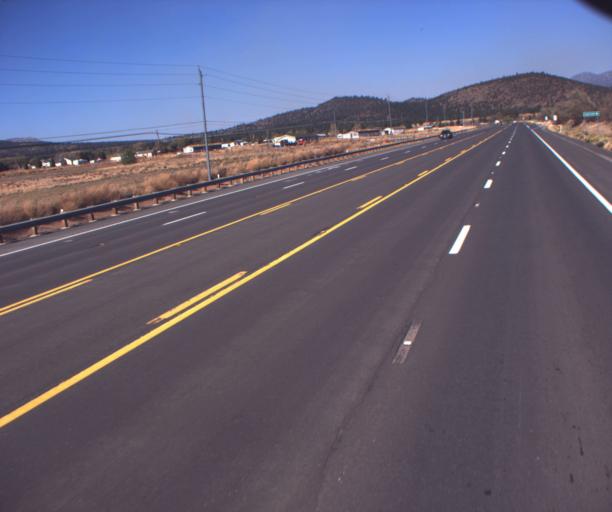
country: US
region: Arizona
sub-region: Coconino County
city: Flagstaff
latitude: 35.3189
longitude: -111.5427
